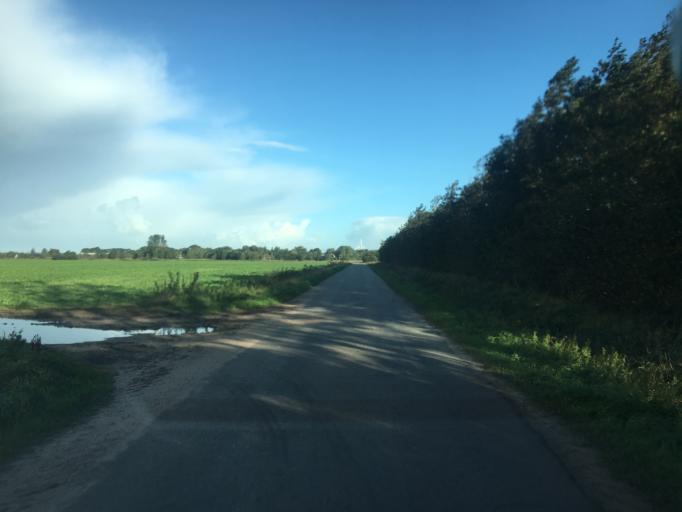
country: DE
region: Schleswig-Holstein
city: Ellhoft
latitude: 54.9557
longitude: 9.0180
